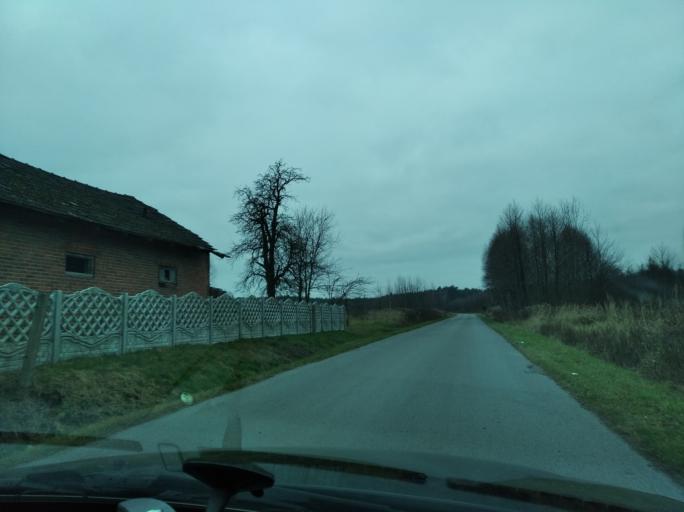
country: PL
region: Subcarpathian Voivodeship
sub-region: Powiat lancucki
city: Brzoza Stadnicka
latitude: 50.1997
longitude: 22.2822
